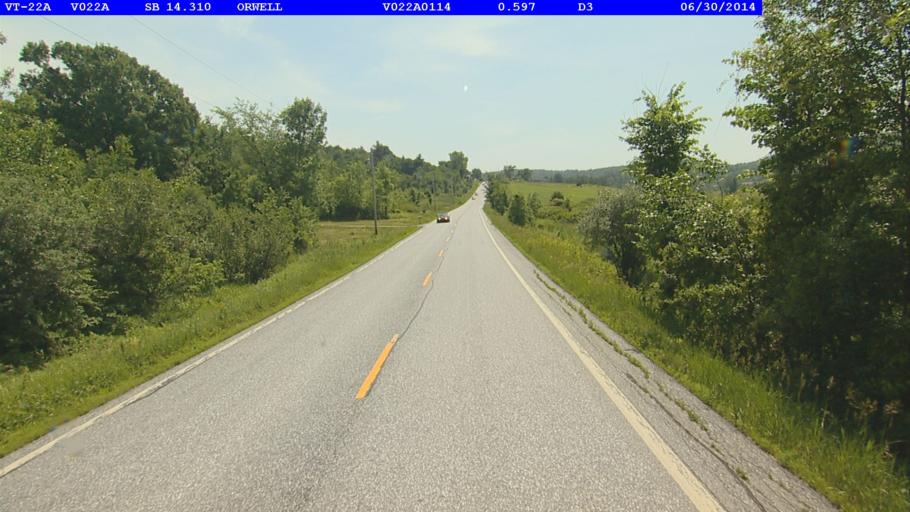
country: US
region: New York
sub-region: Essex County
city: Ticonderoga
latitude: 43.7657
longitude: -73.3105
